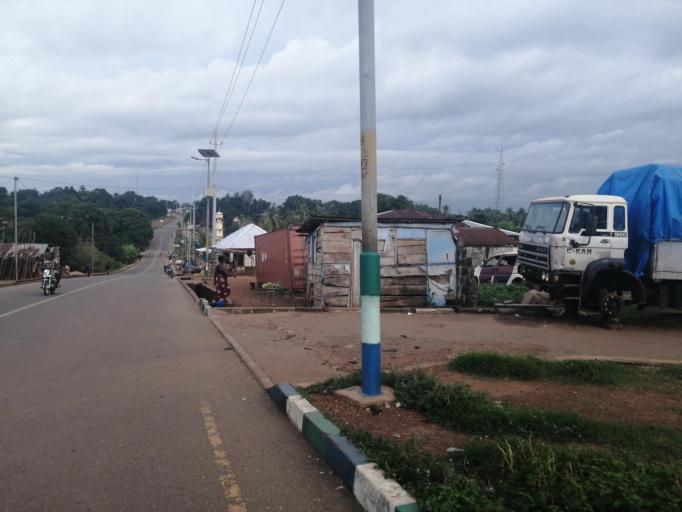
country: SL
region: Northern Province
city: Port Loko
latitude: 8.7714
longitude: -12.7890
